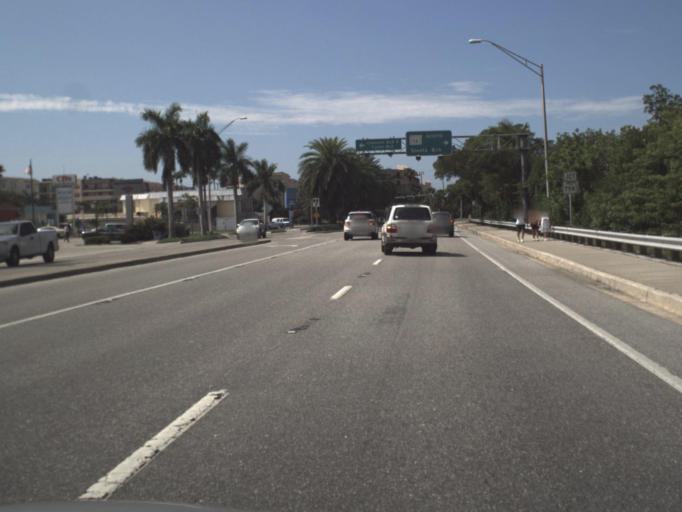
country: US
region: Florida
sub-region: Sarasota County
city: Gulf Gate Estates
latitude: 27.2534
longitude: -82.5338
